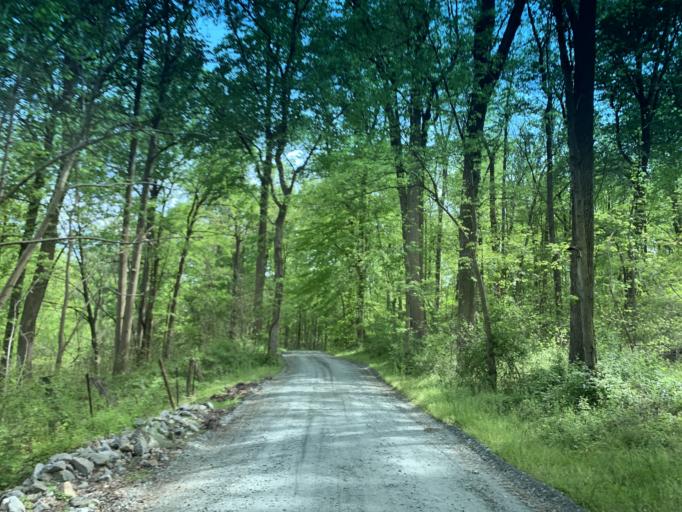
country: US
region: Maryland
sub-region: Harford County
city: South Bel Air
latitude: 39.6200
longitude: -76.2857
